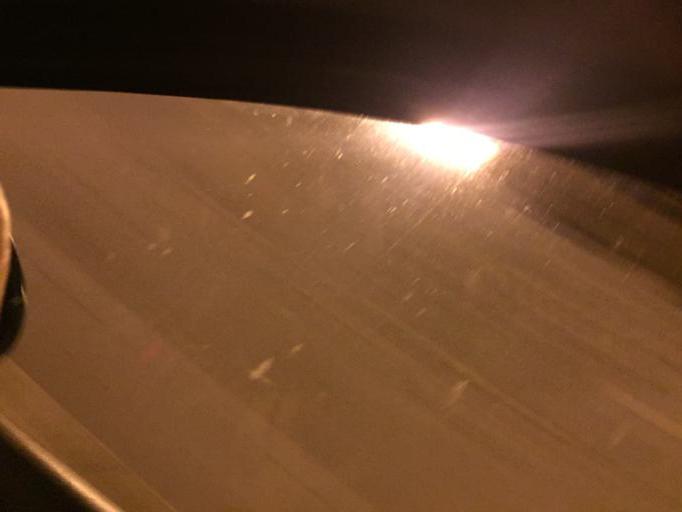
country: MX
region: Veracruz
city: Maltrata
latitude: 18.8275
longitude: -97.2884
